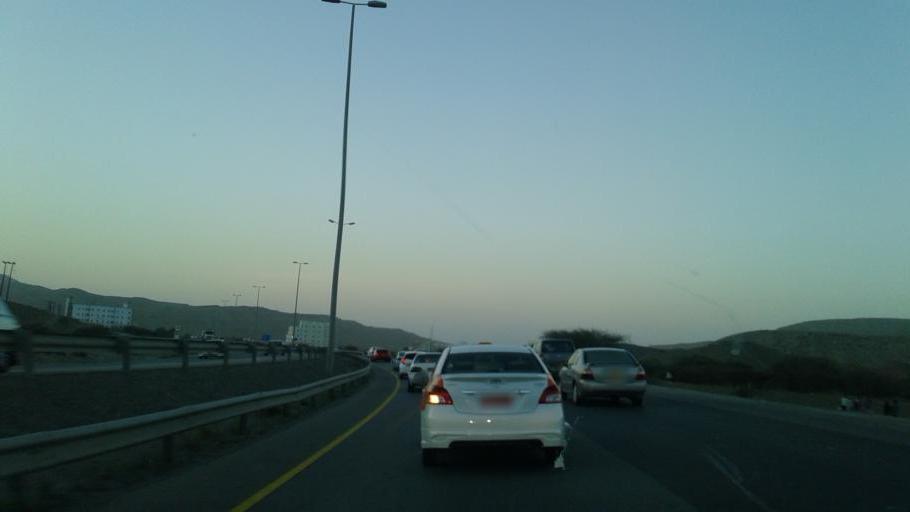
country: OM
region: Muhafazat ad Dakhiliyah
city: Bidbid
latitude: 23.5190
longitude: 58.1925
